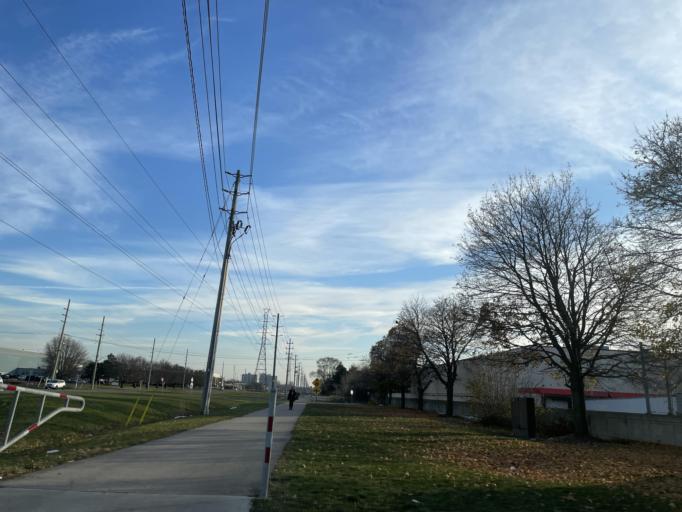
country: CA
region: Ontario
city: Cambridge
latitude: 43.4079
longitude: -80.3220
